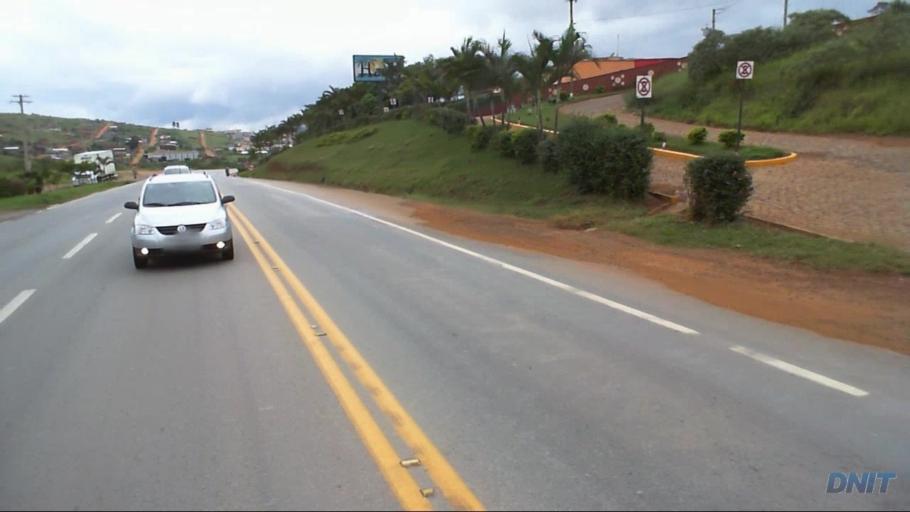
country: BR
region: Minas Gerais
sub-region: Joao Monlevade
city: Joao Monlevade
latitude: -19.8432
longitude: -43.2020
